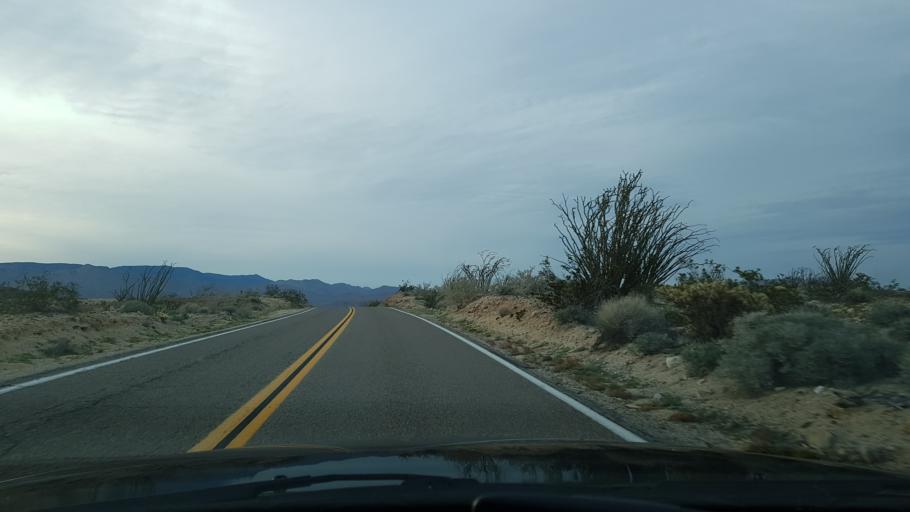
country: MX
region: Baja California
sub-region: Tecate
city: Cereso del Hongo
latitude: 32.8202
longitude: -116.1513
